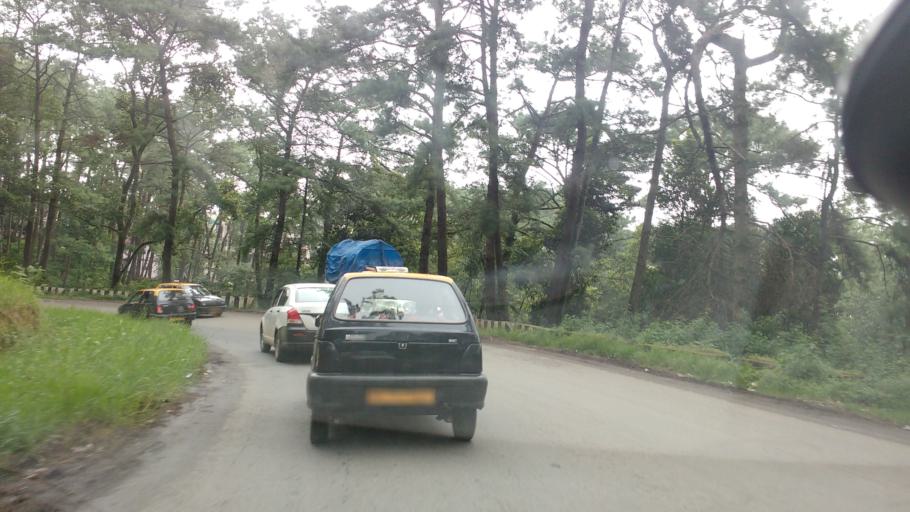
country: IN
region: Meghalaya
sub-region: East Khasi Hills
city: Shillong
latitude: 25.5664
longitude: 91.8581
